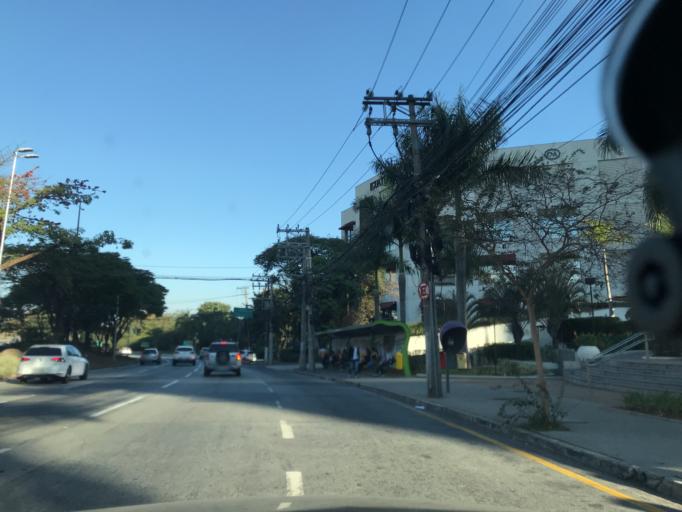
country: BR
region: Sao Paulo
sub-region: Carapicuiba
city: Carapicuiba
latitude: -23.5034
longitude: -46.8478
